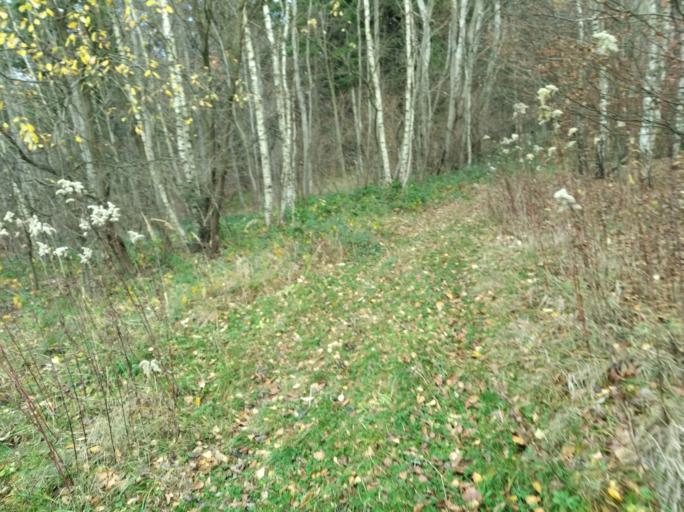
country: PL
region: Subcarpathian Voivodeship
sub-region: Powiat strzyzowski
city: Jawornik
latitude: 49.8579
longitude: 21.8528
